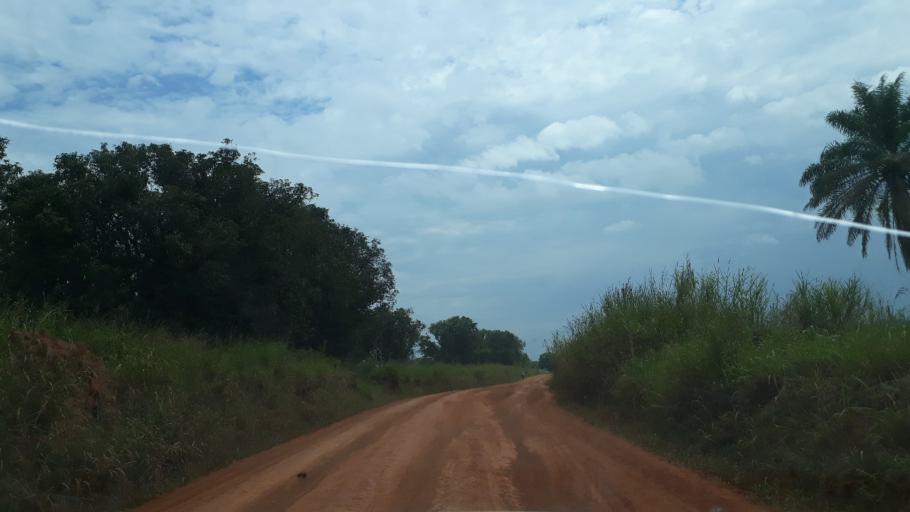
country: CD
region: Eastern Province
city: Bunia
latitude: 1.4645
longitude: 30.0440
